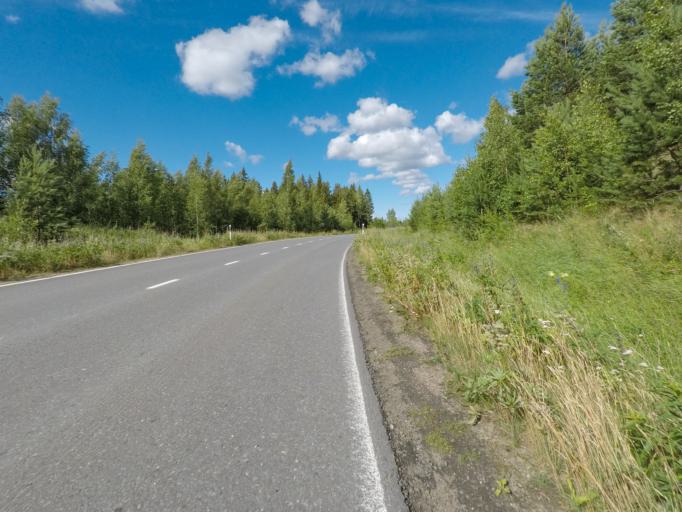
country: FI
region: South Karelia
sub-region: Lappeenranta
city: Joutseno
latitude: 61.0931
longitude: 28.3524
